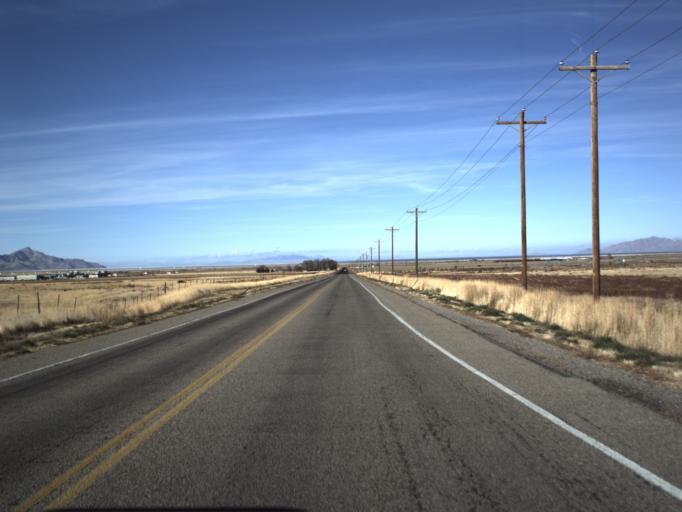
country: US
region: Utah
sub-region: Tooele County
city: Erda
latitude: 40.5891
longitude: -112.3702
